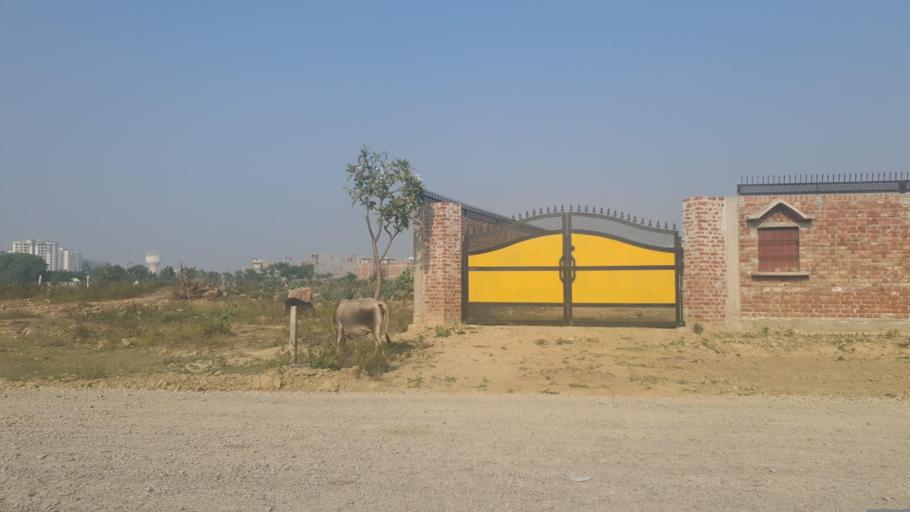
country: IN
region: Uttar Pradesh
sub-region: Lucknow District
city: Goshainganj
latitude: 26.7730
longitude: 81.0095
